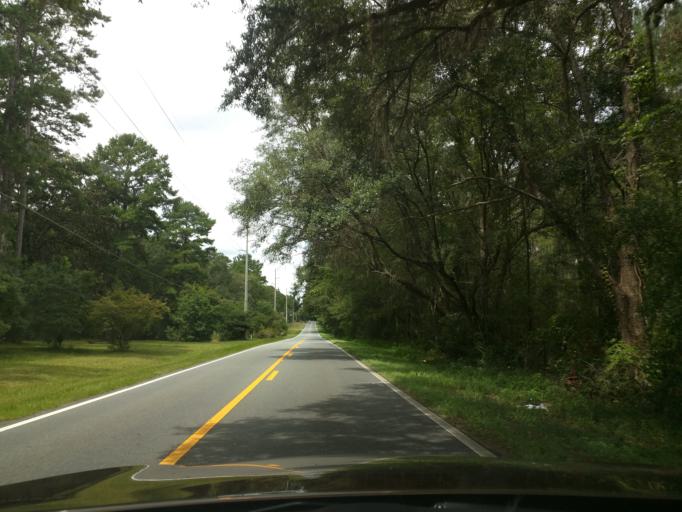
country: US
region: Florida
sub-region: Leon County
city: Tallahassee
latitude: 30.5594
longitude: -84.1846
